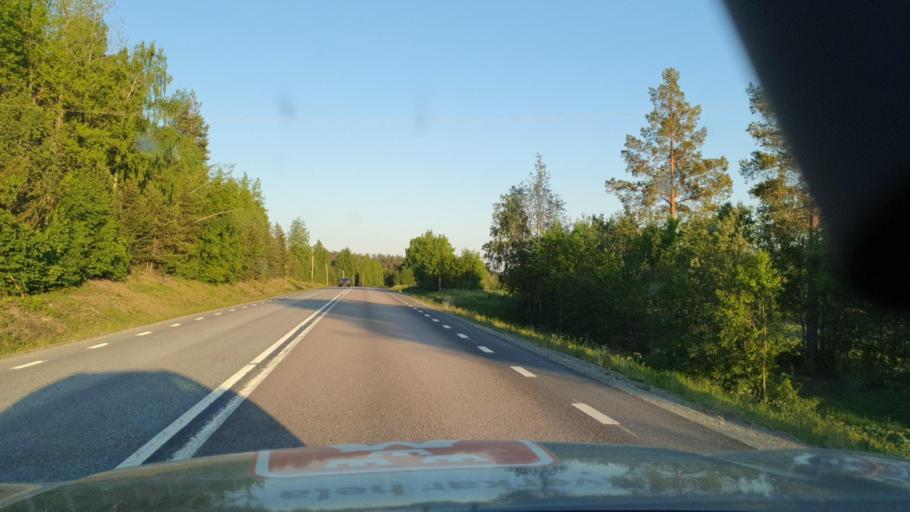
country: SE
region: Vaesternorrland
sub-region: Solleftea Kommun
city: Solleftea
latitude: 63.1953
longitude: 17.2370
